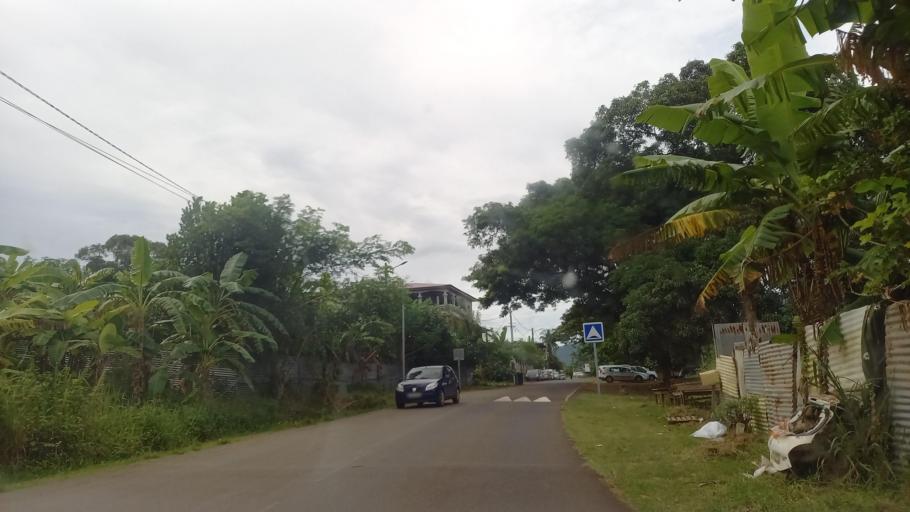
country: YT
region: Boueni
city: Boueni
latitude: -12.9068
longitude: 45.1009
